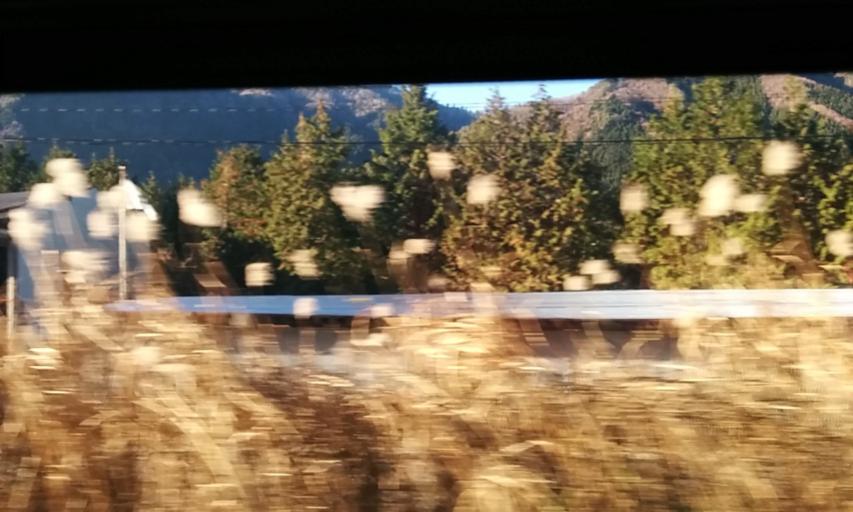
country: JP
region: Nagano
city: Iida
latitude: 35.6777
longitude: 137.6415
